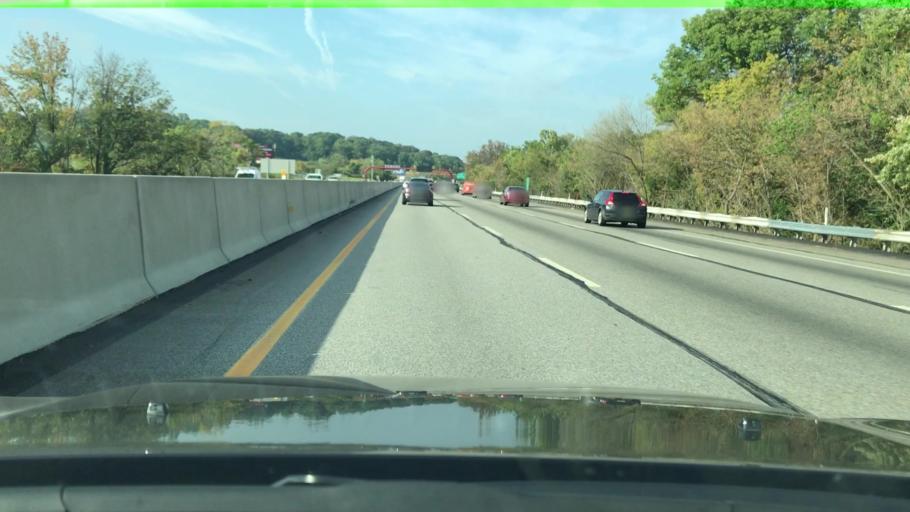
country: US
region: Pennsylvania
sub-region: Montgomery County
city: Plymouth Meeting
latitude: 40.1183
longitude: -75.2576
